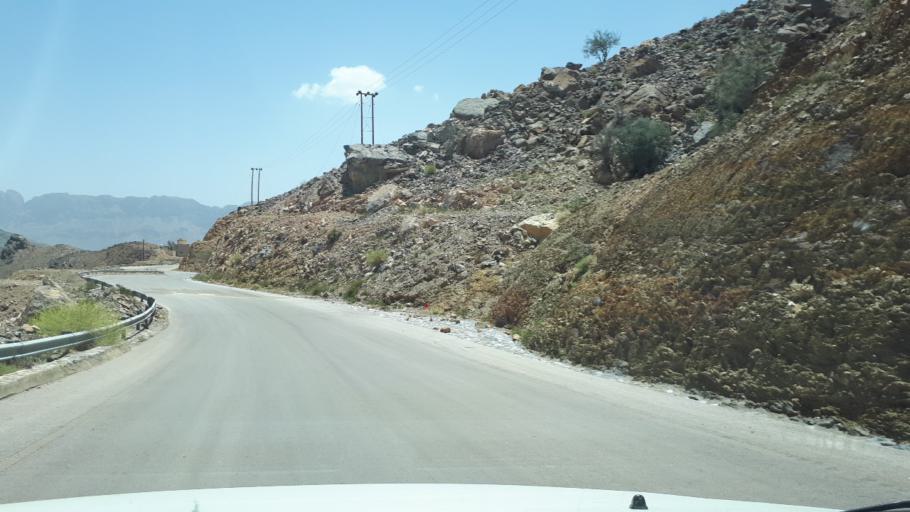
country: OM
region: Muhafazat ad Dakhiliyah
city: Bahla'
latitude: 23.2189
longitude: 57.1457
